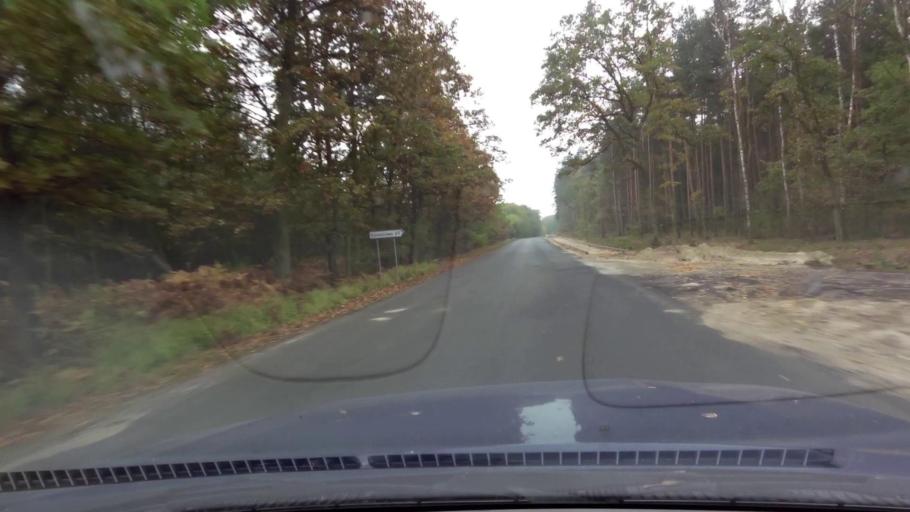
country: PL
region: West Pomeranian Voivodeship
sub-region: Powiat goleniowski
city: Goleniow
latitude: 53.5136
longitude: 14.7442
